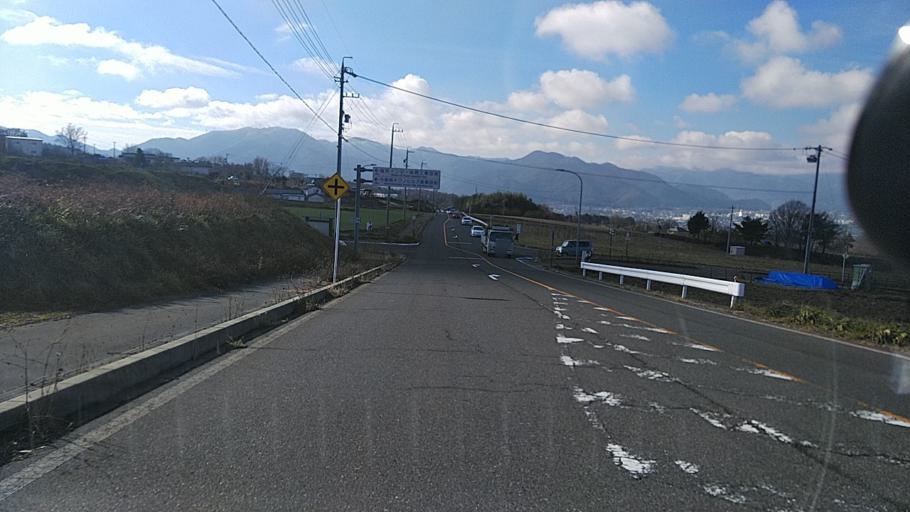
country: JP
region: Nagano
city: Shiojiri
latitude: 36.1320
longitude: 137.9872
